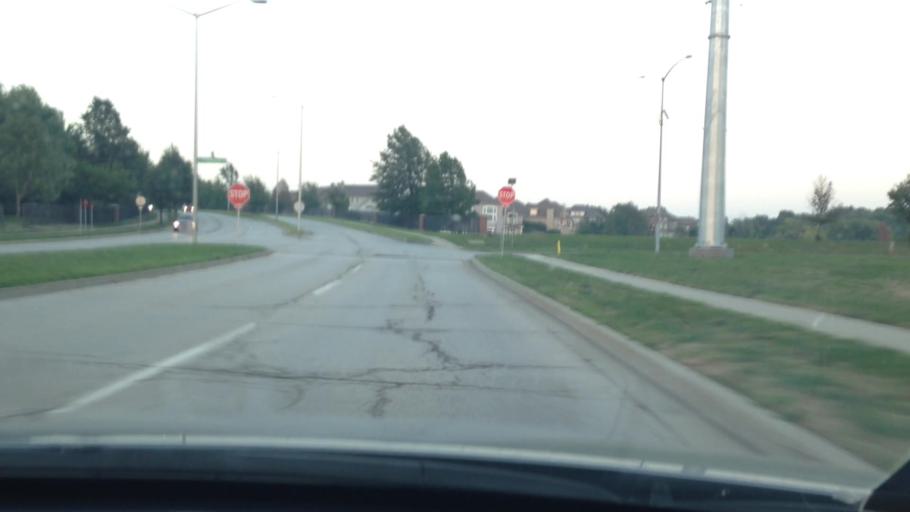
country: US
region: Missouri
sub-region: Clay County
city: Liberty
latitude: 39.2667
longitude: -94.4666
